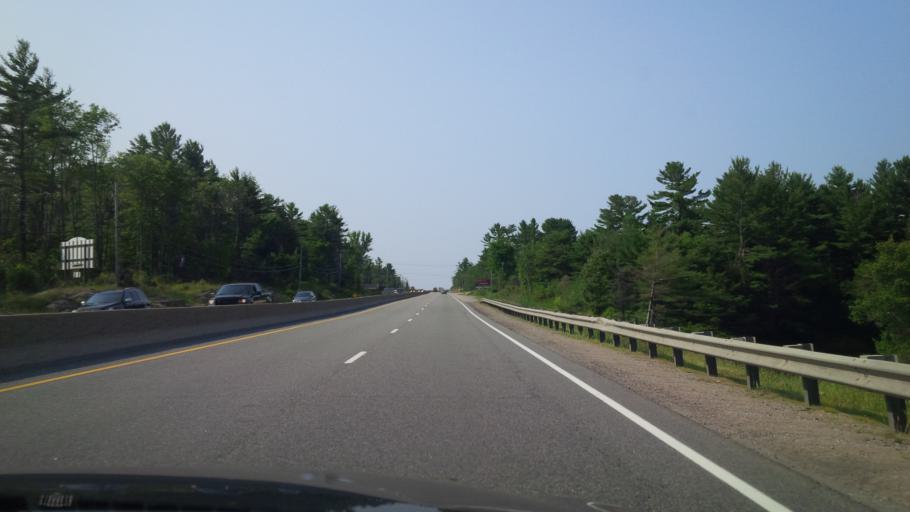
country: CA
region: Ontario
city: Gravenhurst
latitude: 44.8306
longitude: -79.3211
